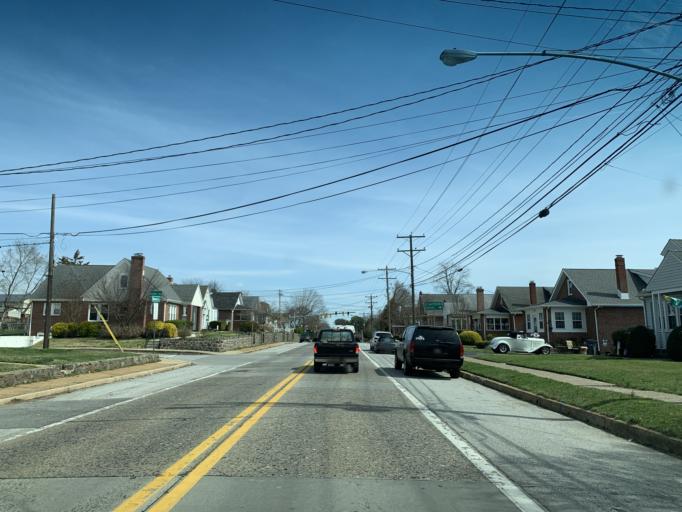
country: US
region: Delaware
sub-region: New Castle County
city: Newport
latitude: 39.7234
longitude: -75.5977
